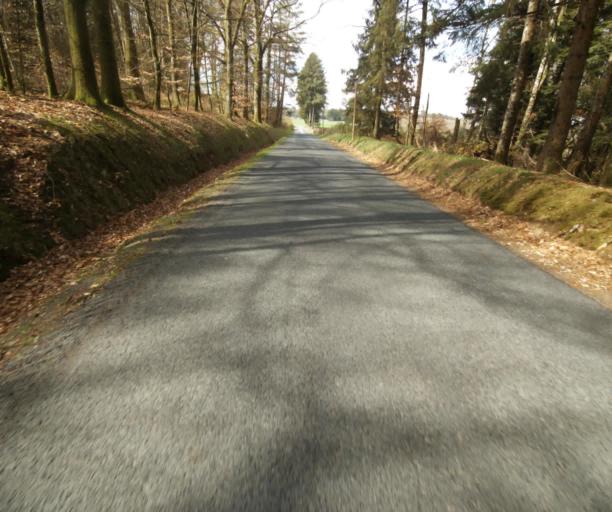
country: FR
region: Limousin
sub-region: Departement de la Correze
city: Correze
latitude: 45.3502
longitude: 1.8995
